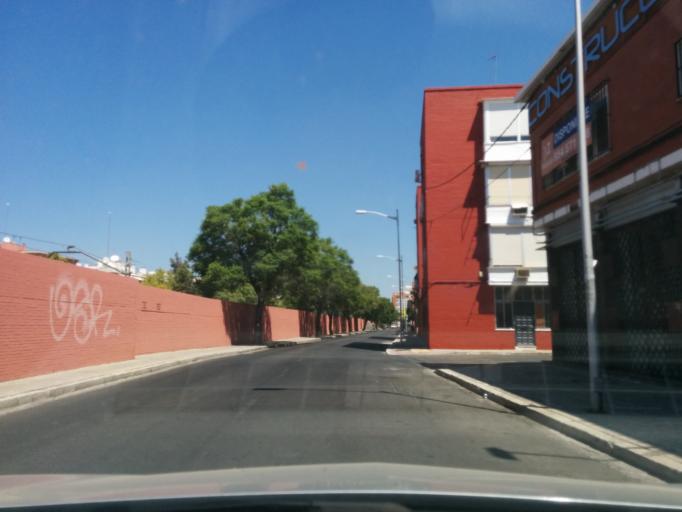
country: ES
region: Andalusia
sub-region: Provincia de Sevilla
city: Sevilla
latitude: 37.3665
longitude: -5.9771
